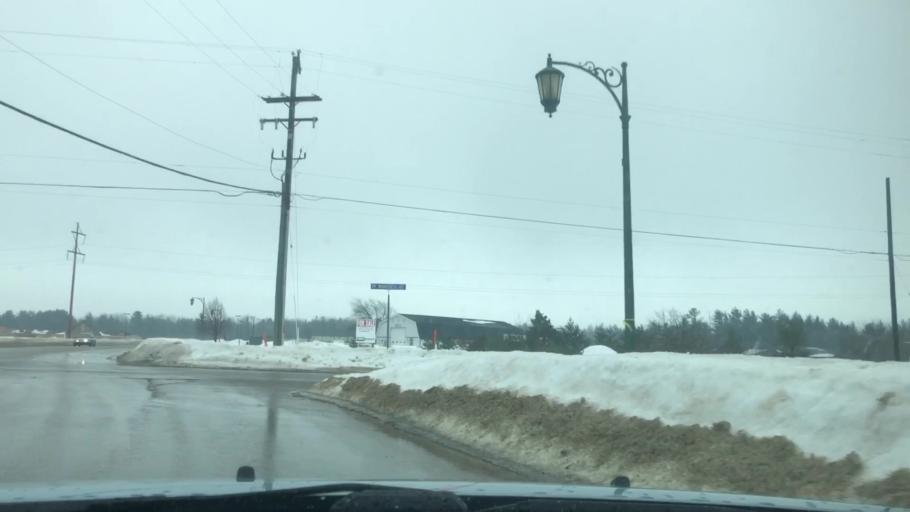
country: US
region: Michigan
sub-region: Otsego County
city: Gaylord
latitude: 45.0265
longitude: -84.6943
